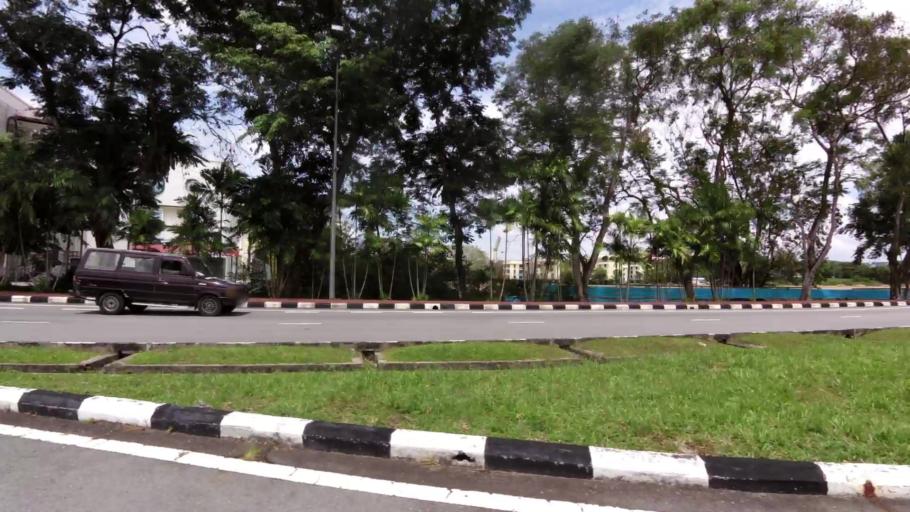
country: BN
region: Brunei and Muara
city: Bandar Seri Begawan
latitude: 4.9328
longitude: 114.9411
